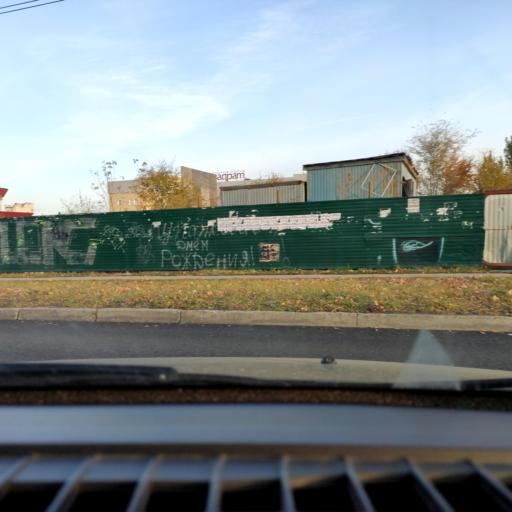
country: RU
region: Samara
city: Tol'yatti
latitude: 53.5147
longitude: 49.2830
